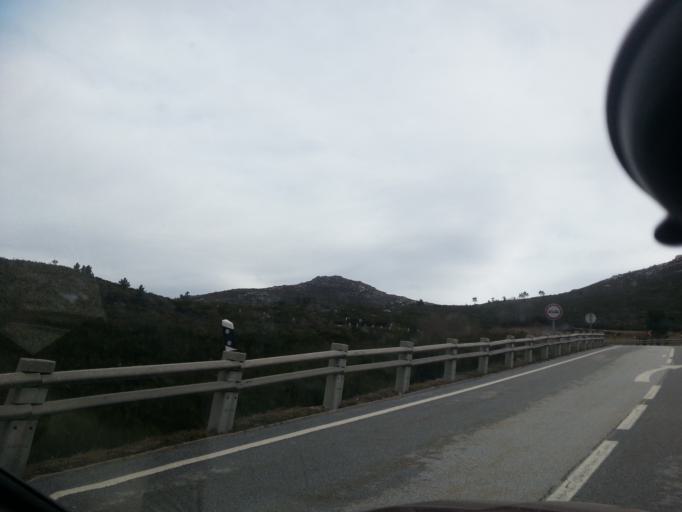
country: PT
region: Guarda
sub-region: Seia
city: Seia
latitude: 40.3479
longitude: -7.7063
